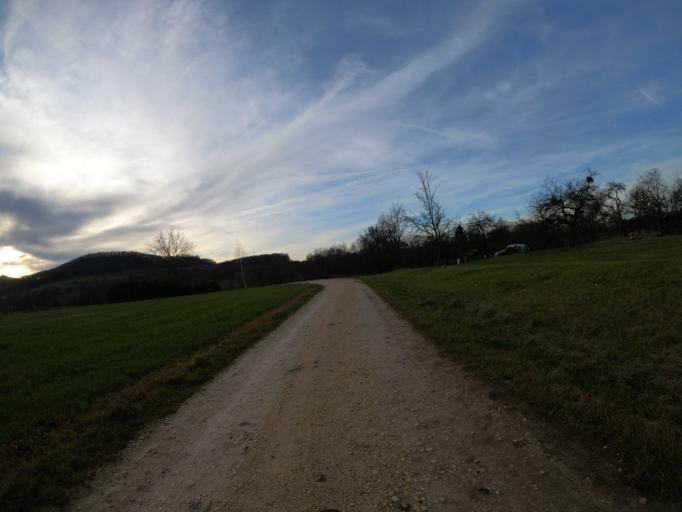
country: DE
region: Baden-Wuerttemberg
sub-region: Regierungsbezirk Stuttgart
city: Zell unter Aichelberg
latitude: 48.6393
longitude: 9.5905
